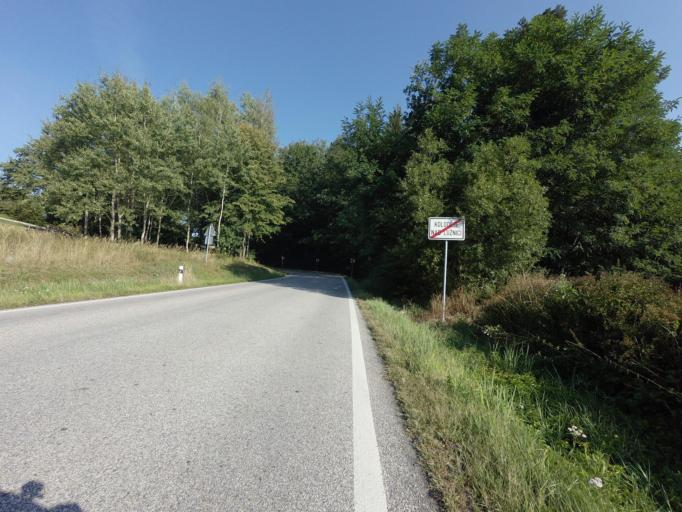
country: CZ
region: Jihocesky
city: Tyn nad Vltavou
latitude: 49.2548
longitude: 14.4194
